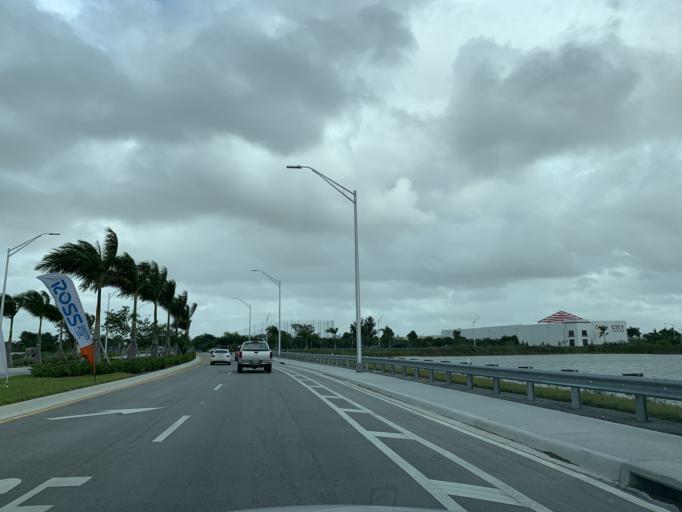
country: US
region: Florida
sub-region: Miami-Dade County
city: Tamiami
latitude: 25.7846
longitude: -80.3907
